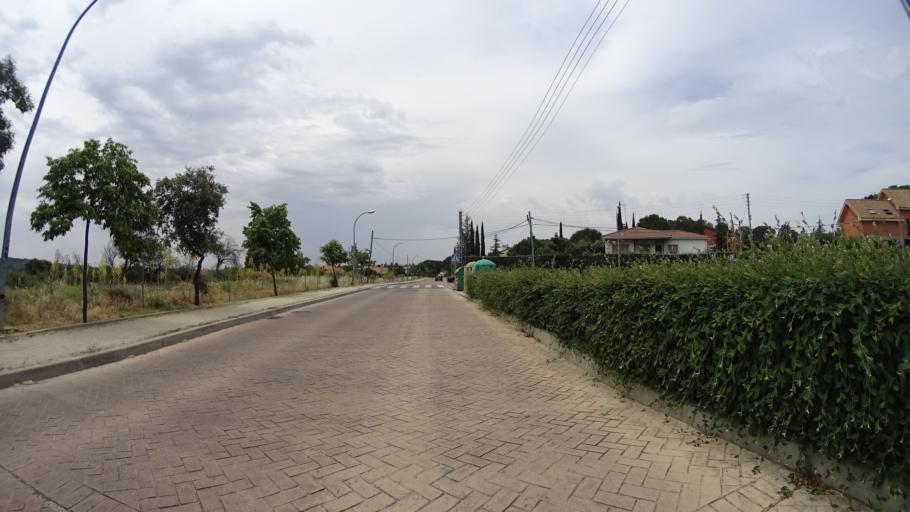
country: ES
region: Madrid
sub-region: Provincia de Madrid
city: Colmenarejo
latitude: 40.5665
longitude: -4.0098
